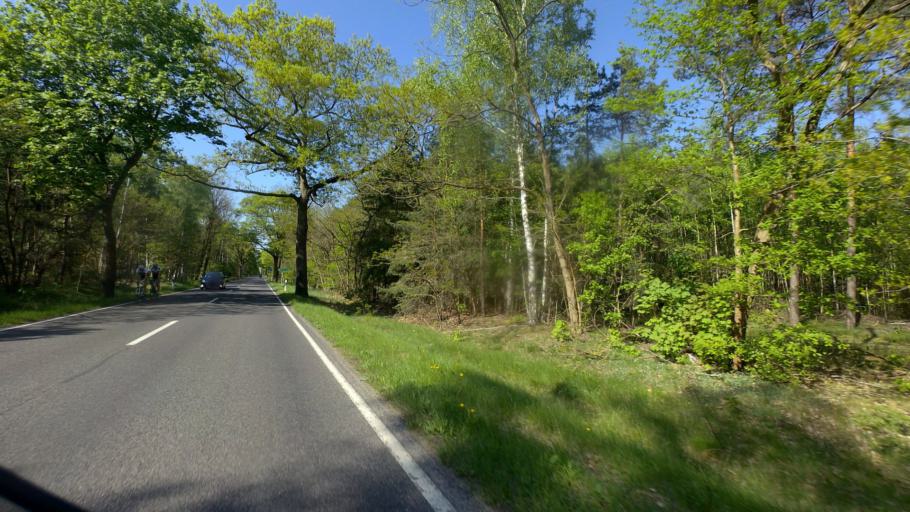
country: DE
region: Brandenburg
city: Gross Koris
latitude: 52.1925
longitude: 13.6972
